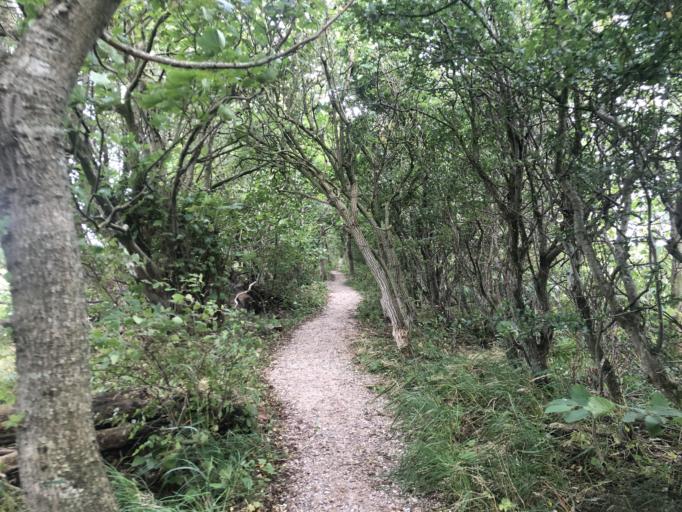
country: DK
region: Central Jutland
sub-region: Ringkobing-Skjern Kommune
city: Skjern
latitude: 55.9035
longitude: 8.4229
